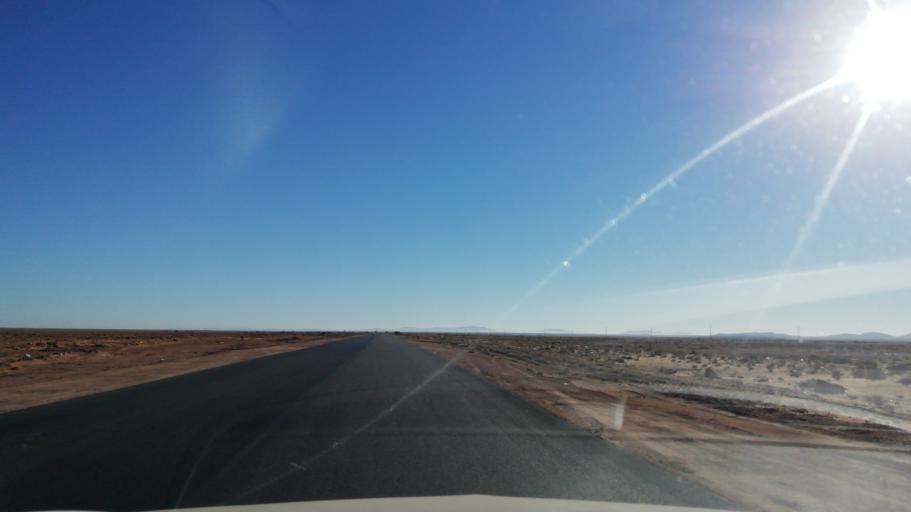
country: DZ
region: El Bayadh
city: El Bayadh
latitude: 33.8579
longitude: 0.5763
